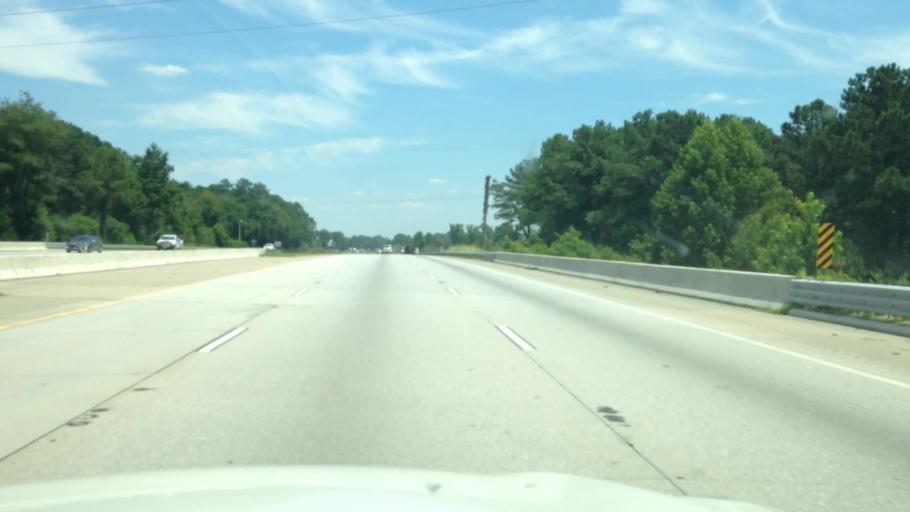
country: US
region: South Carolina
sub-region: Florence County
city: Florence
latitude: 34.2648
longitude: -79.7321
